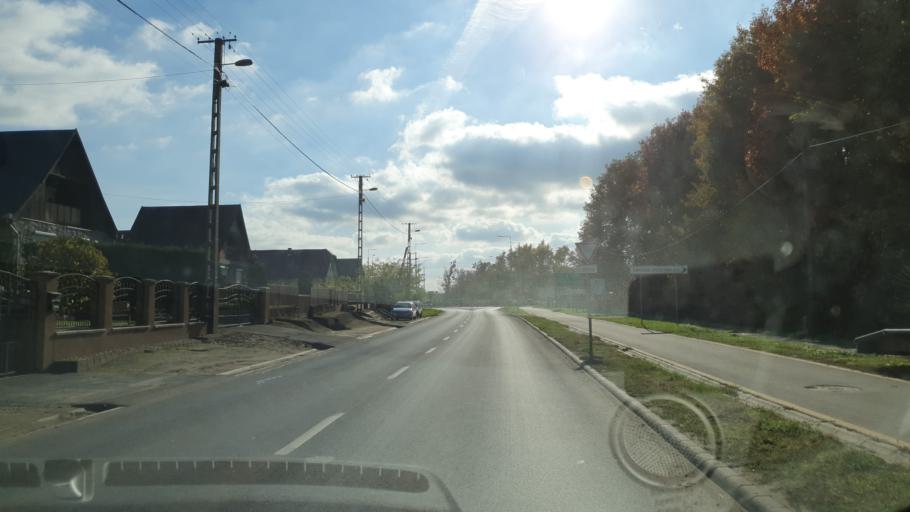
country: HU
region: Szabolcs-Szatmar-Bereg
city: Kisvarda
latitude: 48.2026
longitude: 22.0915
